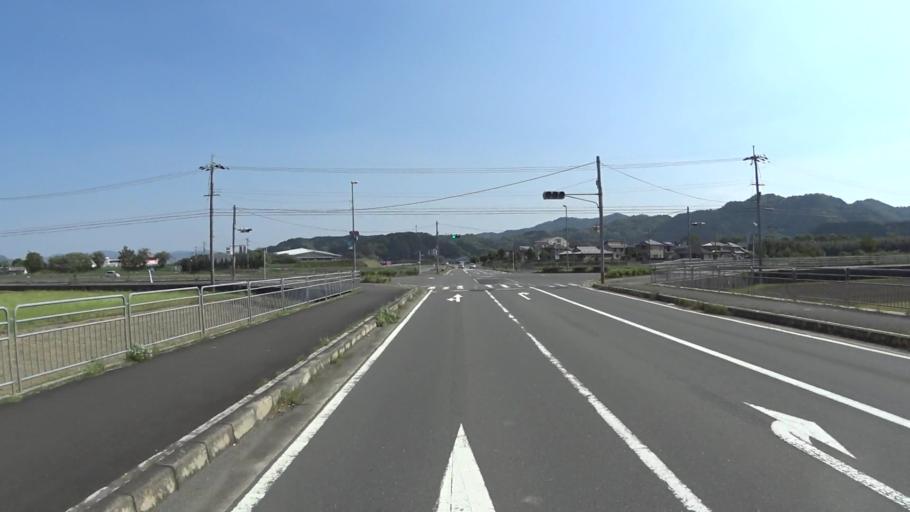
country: JP
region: Kyoto
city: Kameoka
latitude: 35.0781
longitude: 135.5370
